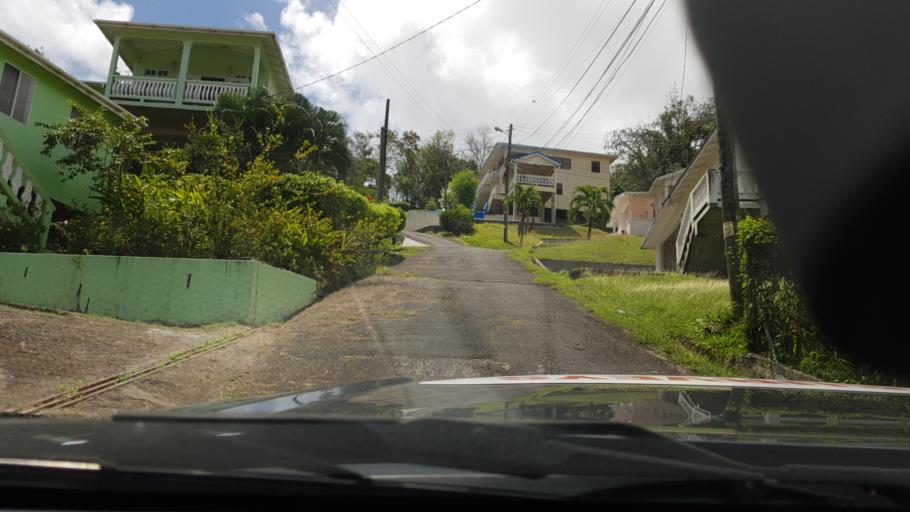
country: LC
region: Gros-Islet
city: Gros Islet
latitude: 14.0678
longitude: -60.9350
